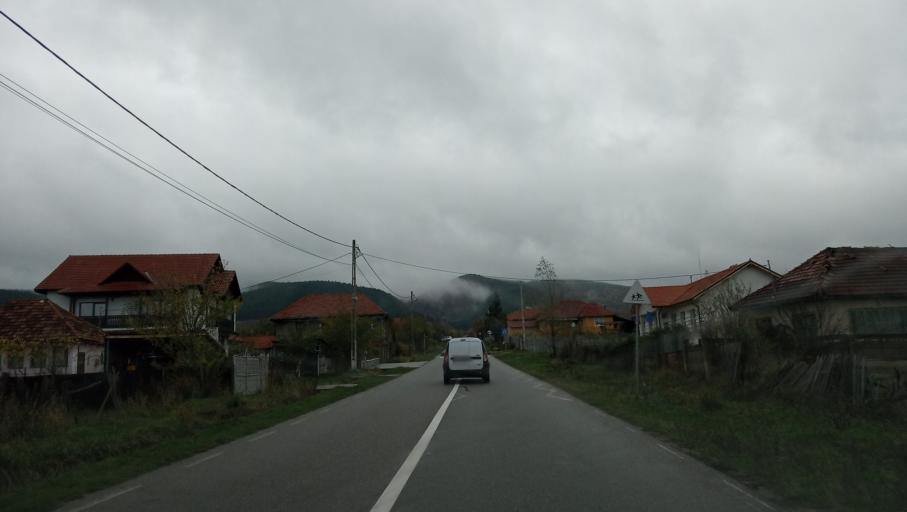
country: RO
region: Gorj
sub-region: Comuna Crasna
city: Crasna
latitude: 45.1700
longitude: 23.4840
